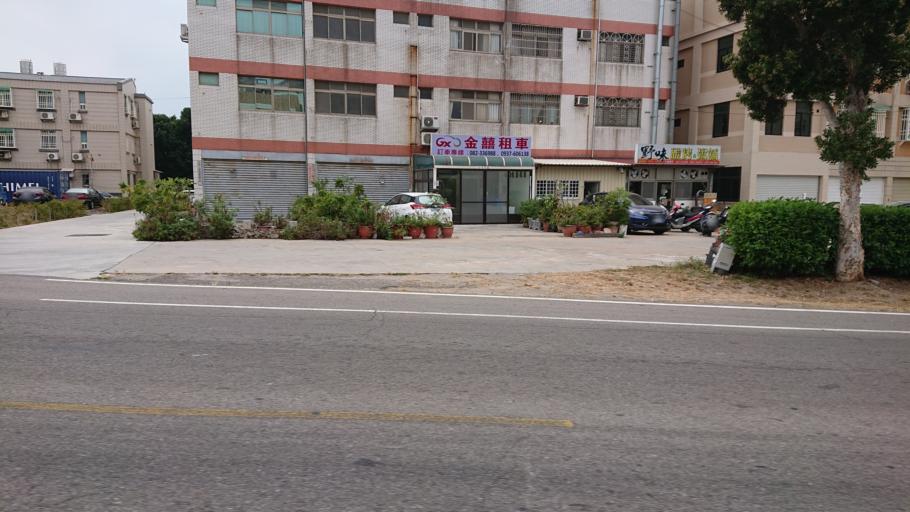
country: TW
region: Fukien
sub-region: Kinmen
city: Jincheng
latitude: 24.4374
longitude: 118.4078
